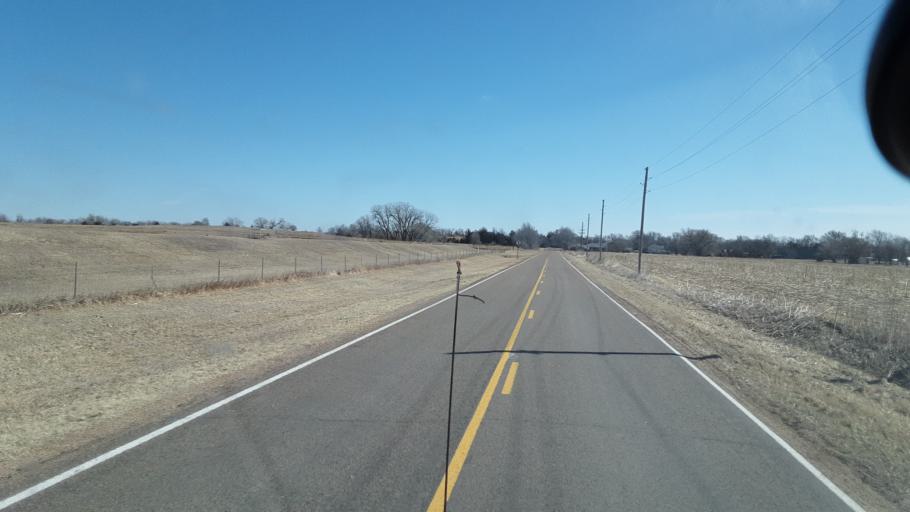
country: US
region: Kansas
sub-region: Barton County
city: Ellinwood
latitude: 38.2821
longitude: -98.4236
